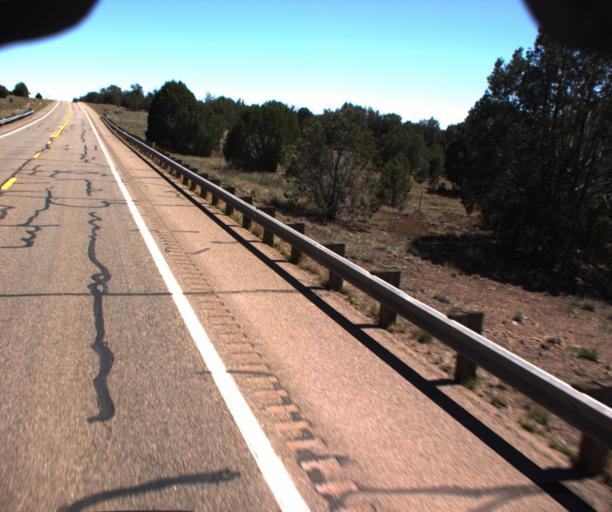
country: US
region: Arizona
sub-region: Yavapai County
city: Paulden
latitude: 35.1217
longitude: -112.4348
